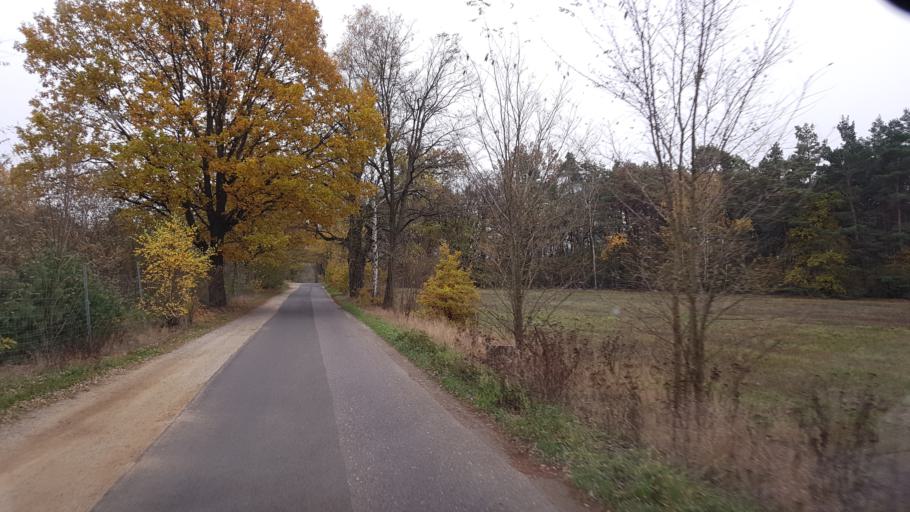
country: DE
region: Brandenburg
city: Crinitz
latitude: 51.7161
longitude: 13.7823
